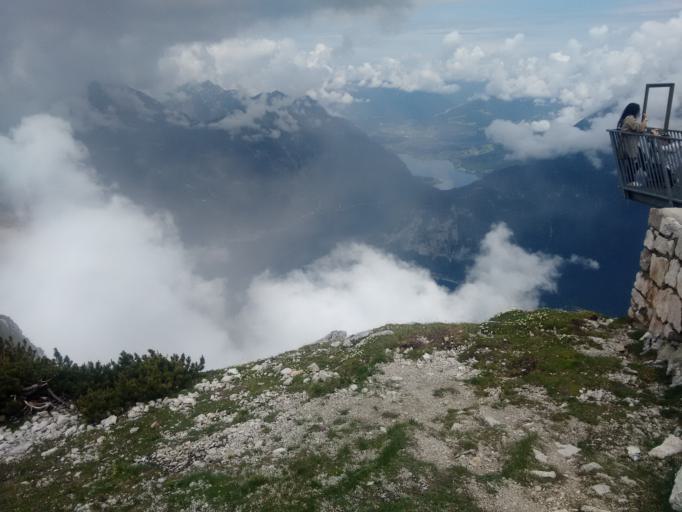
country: AT
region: Styria
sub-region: Politischer Bezirk Liezen
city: Bad Aussee
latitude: 47.5285
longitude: 13.6920
